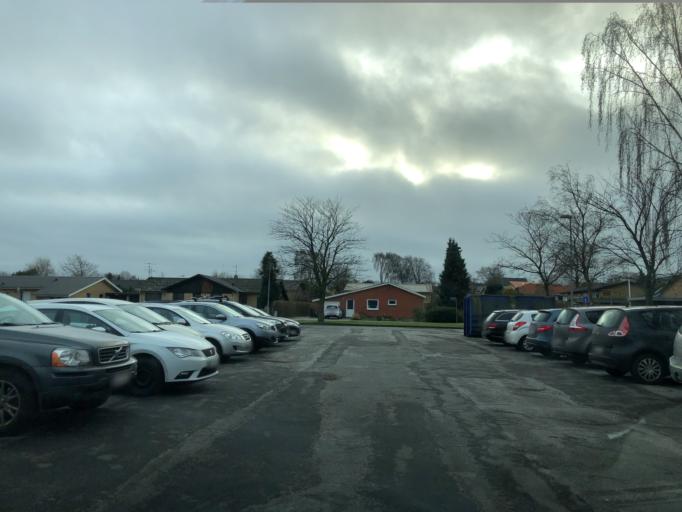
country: DK
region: Central Jutland
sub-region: Viborg Kommune
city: Stoholm
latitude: 56.4835
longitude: 9.1469
